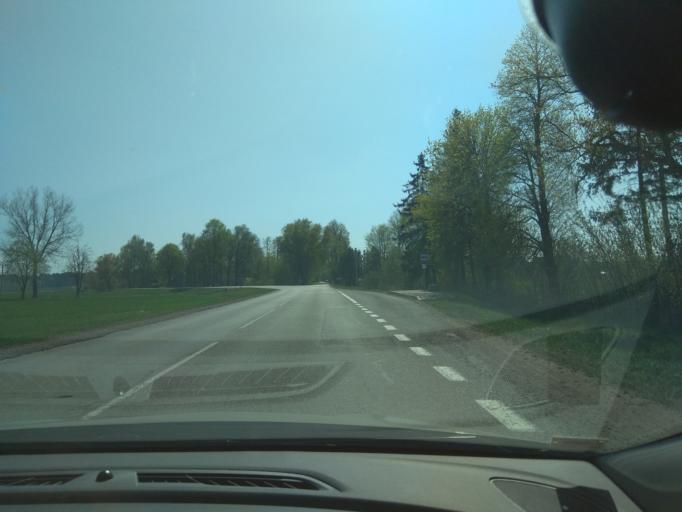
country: LT
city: Linkuva
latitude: 56.0047
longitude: 24.1617
